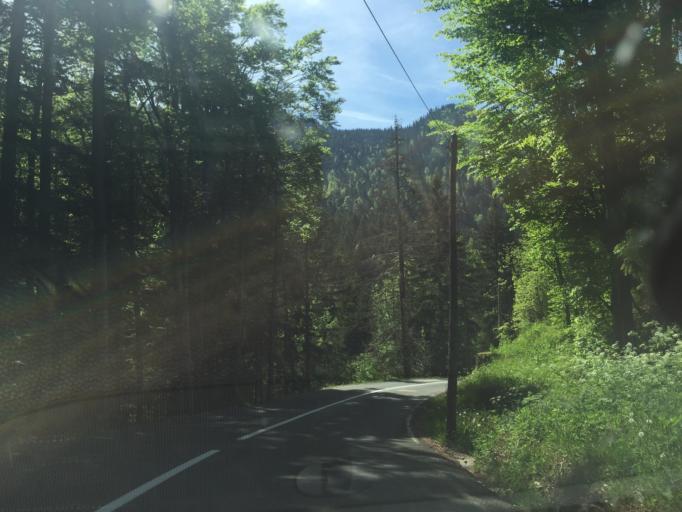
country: FR
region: Rhone-Alpes
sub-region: Departement de l'Isere
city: Saint-Hilaire
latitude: 45.3714
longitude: 5.8387
